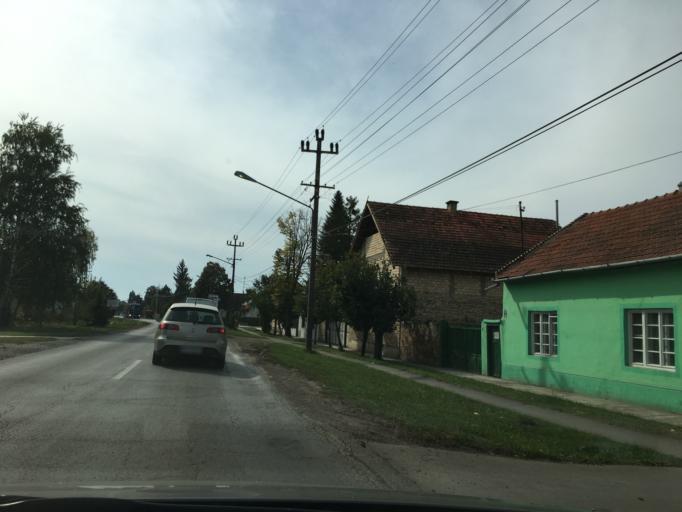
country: RS
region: Autonomna Pokrajina Vojvodina
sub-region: Juznobacki Okrug
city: Temerin
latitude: 45.4264
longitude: 19.8948
